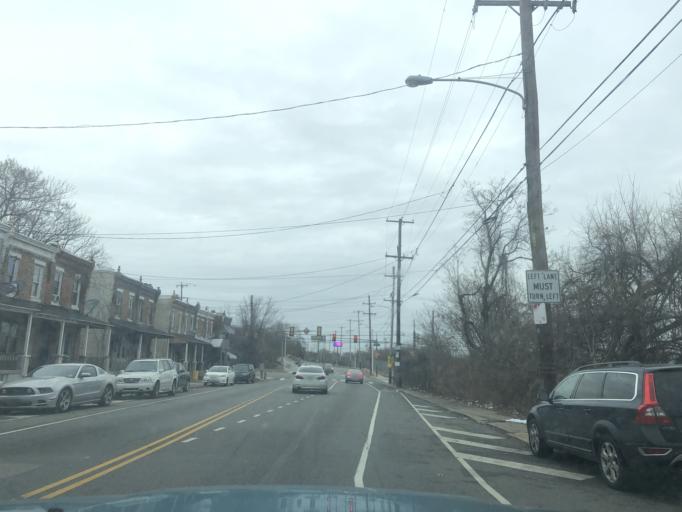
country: US
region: Pennsylvania
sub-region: Philadelphia County
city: Philadelphia
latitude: 40.0148
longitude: -75.1709
